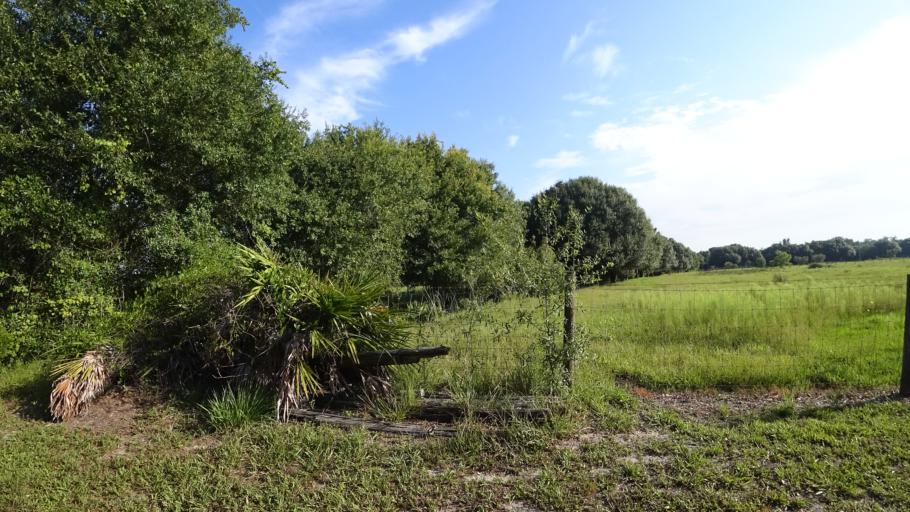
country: US
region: Florida
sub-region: Sarasota County
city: Lake Sarasota
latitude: 27.3593
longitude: -82.1653
